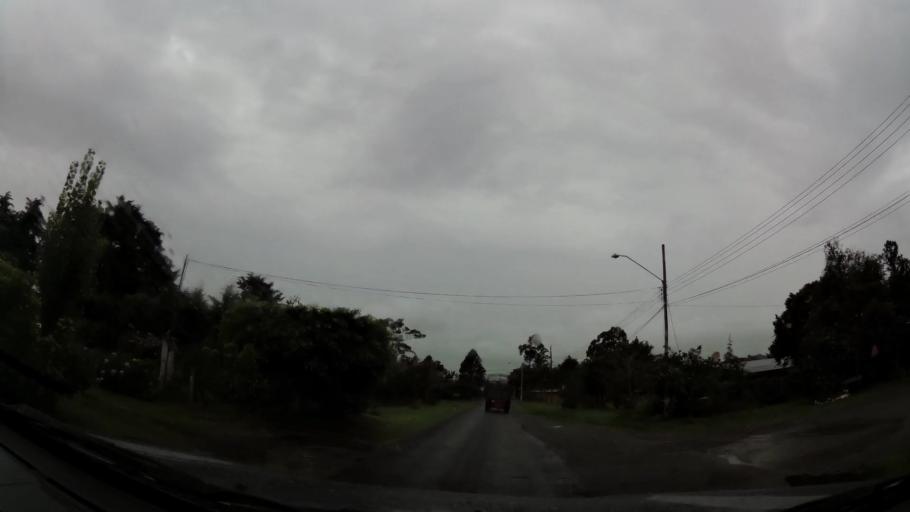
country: PA
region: Chiriqui
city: Volcan
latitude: 8.7902
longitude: -82.6481
